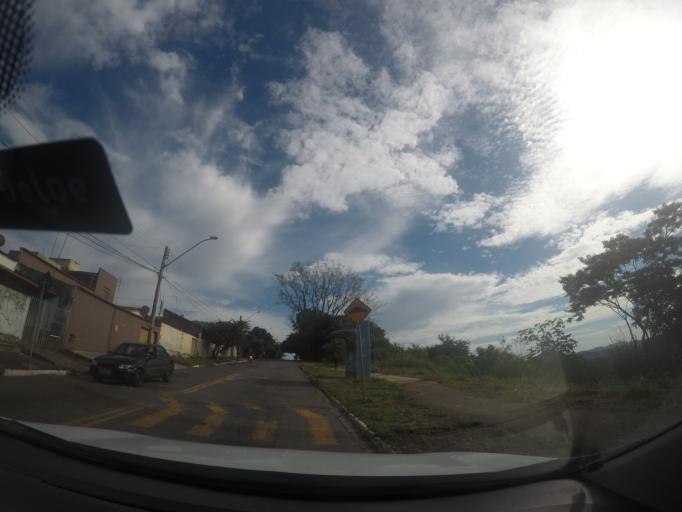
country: BR
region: Goias
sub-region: Goiania
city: Goiania
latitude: -16.6912
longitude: -49.2038
